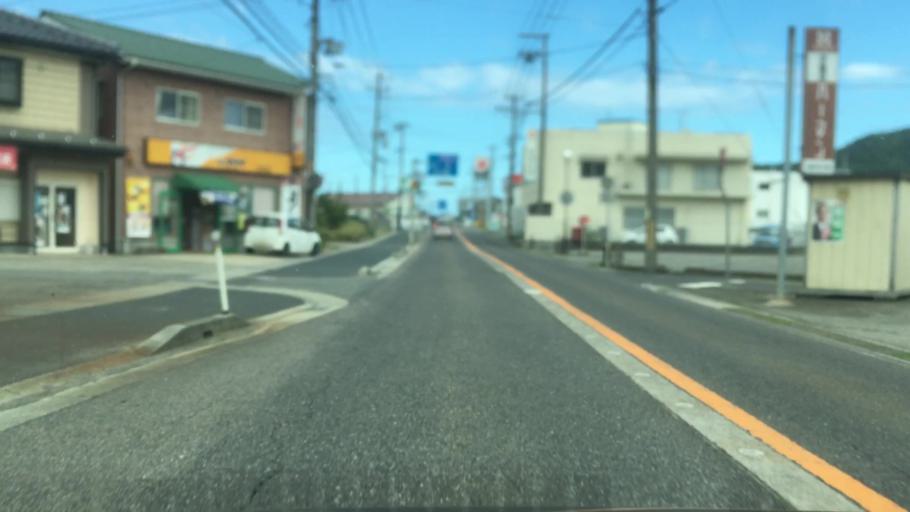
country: JP
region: Tottori
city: Tottori
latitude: 35.6182
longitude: 134.4626
